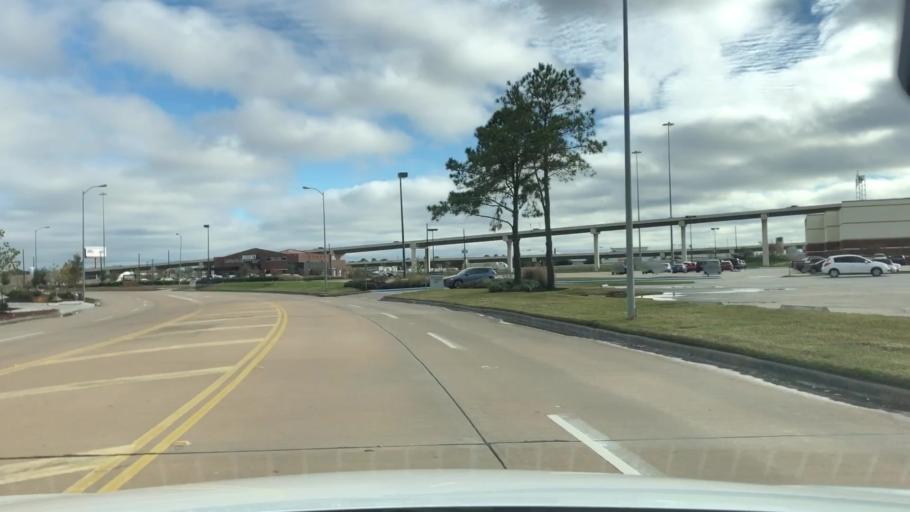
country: US
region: Texas
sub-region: Harris County
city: Katy
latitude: 29.7887
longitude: -95.7738
